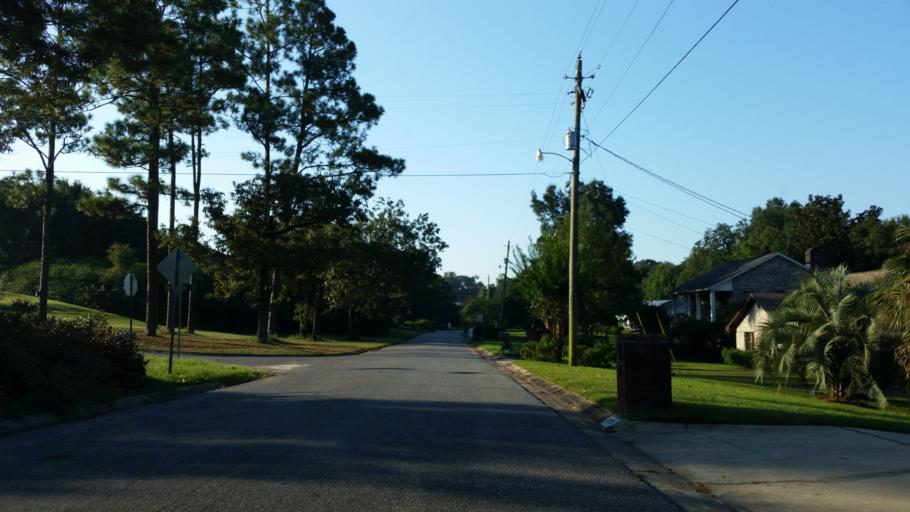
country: US
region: Florida
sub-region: Escambia County
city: Ferry Pass
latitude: 30.5405
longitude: -87.2292
